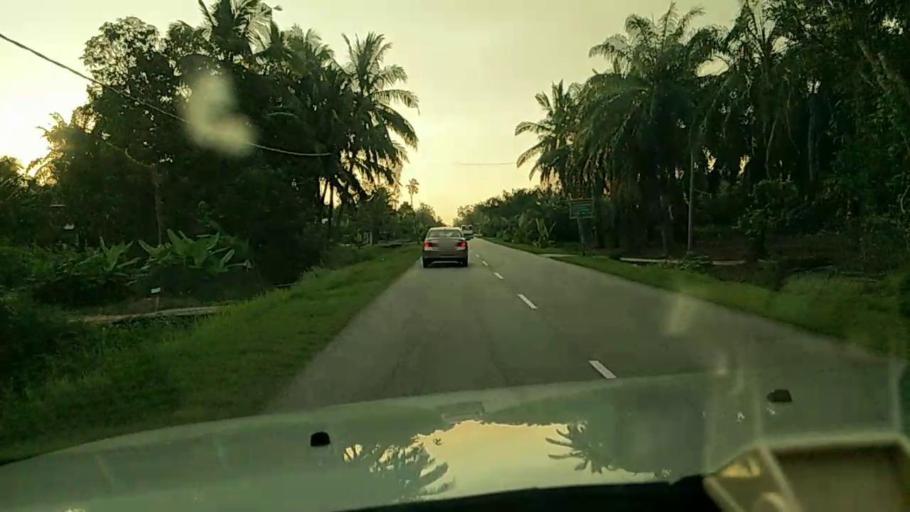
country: MY
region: Selangor
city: Kuala Selangor
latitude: 3.3089
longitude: 101.2907
